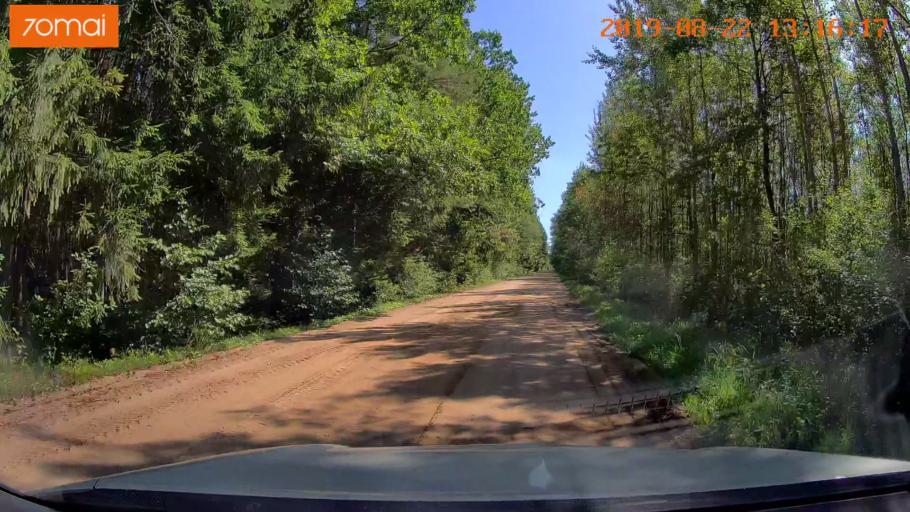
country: BY
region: Minsk
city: Prawdzinski
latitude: 53.2567
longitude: 27.9094
